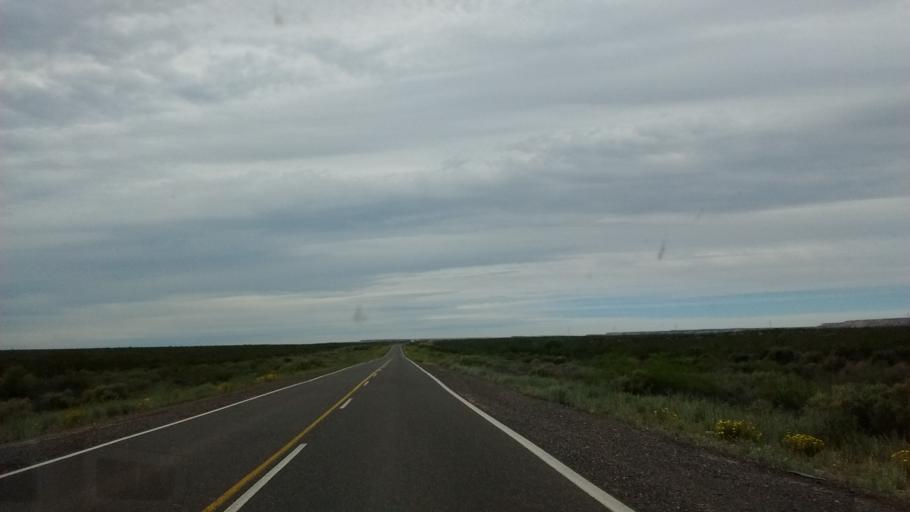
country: AR
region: Rio Negro
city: Catriel
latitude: -38.1157
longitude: -67.9305
